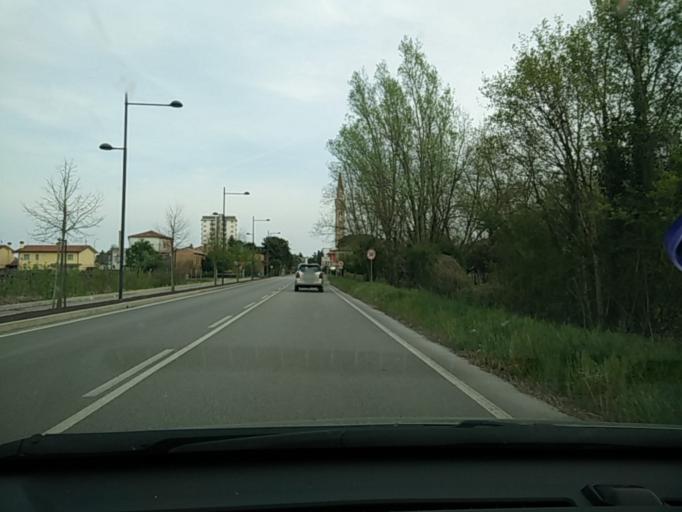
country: IT
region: Veneto
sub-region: Provincia di Venezia
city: Noventa di Piave
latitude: 45.6648
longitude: 12.5255
